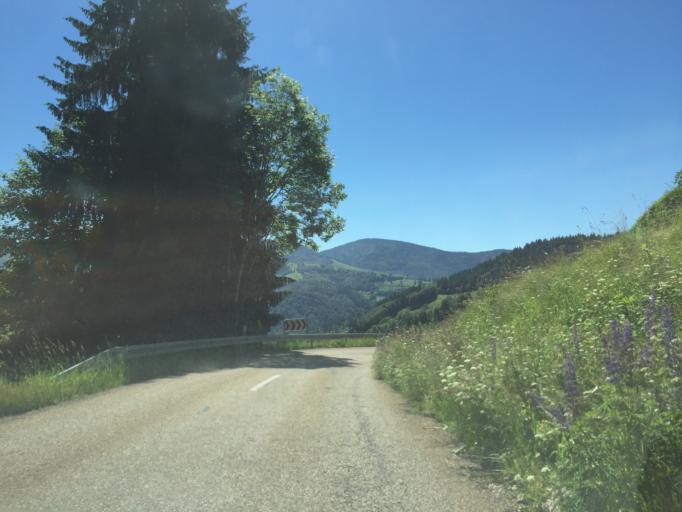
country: DE
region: Baden-Wuerttemberg
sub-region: Freiburg Region
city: Schonenberg
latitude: 47.8094
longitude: 7.8801
